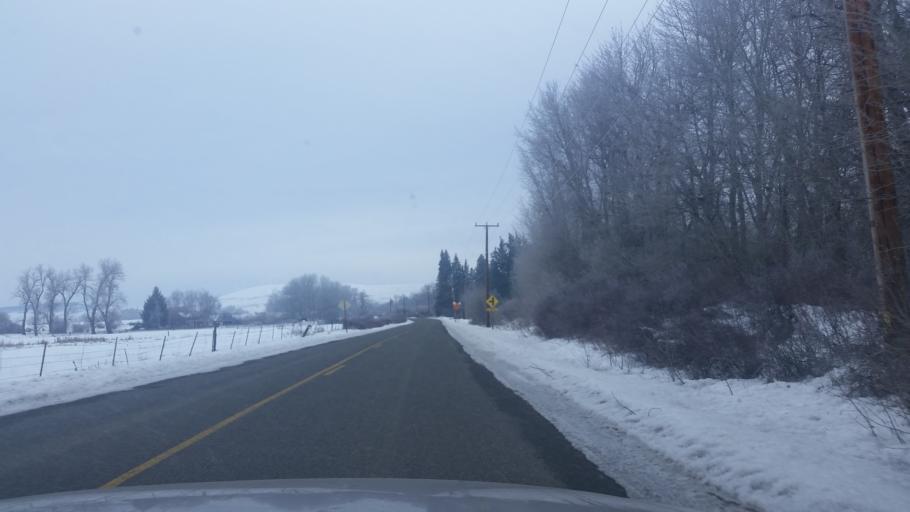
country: US
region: Washington
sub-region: Kittitas County
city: Ellensburg
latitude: 47.0776
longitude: -120.6873
